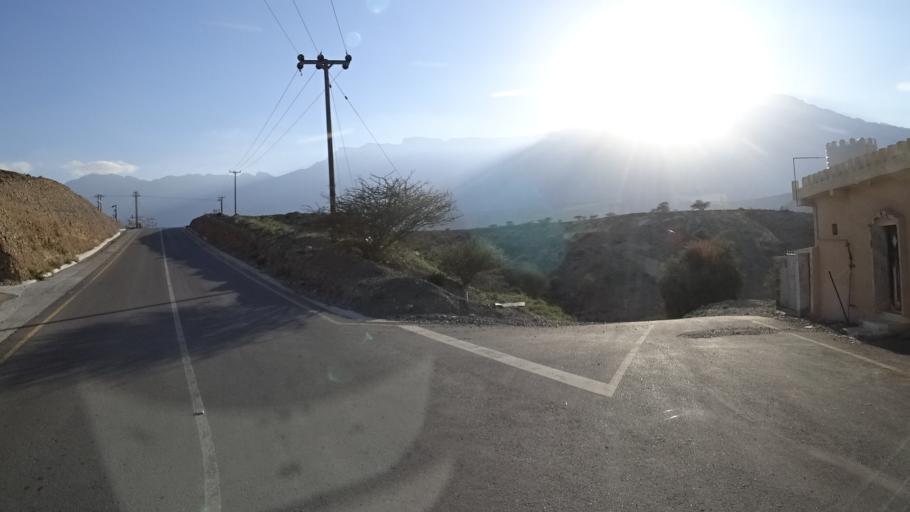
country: OM
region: Al Batinah
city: Rustaq
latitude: 23.2838
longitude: 57.3294
